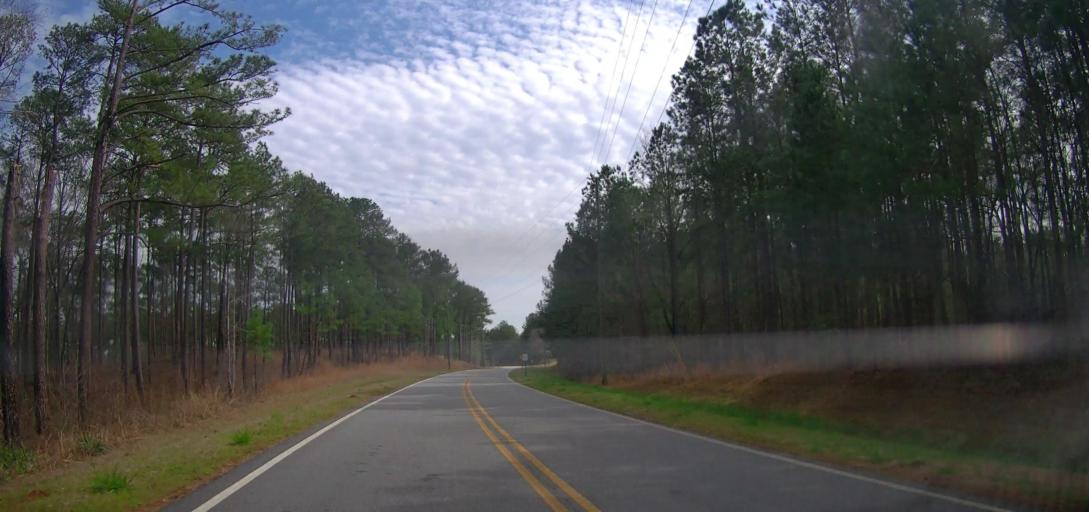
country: US
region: Georgia
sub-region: Jones County
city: Gray
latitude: 33.0673
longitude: -83.7297
